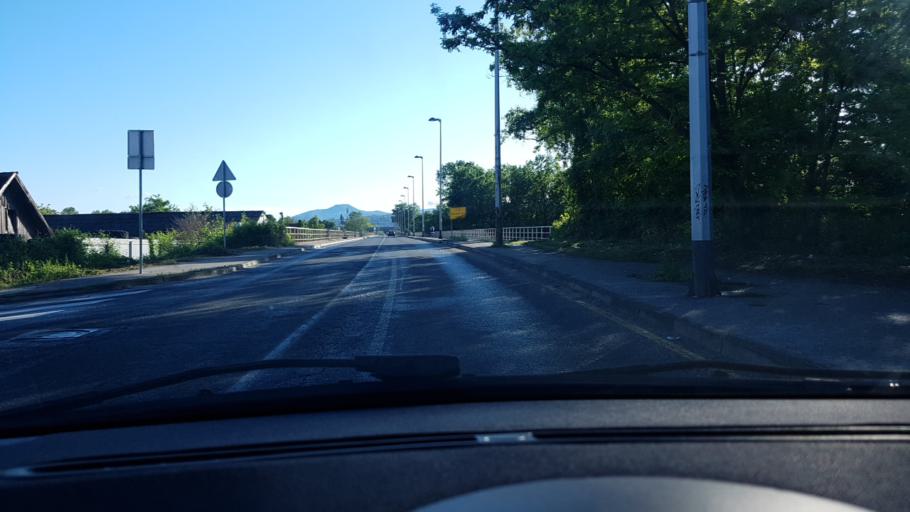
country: HR
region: Zagrebacka
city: Bestovje
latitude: 45.8149
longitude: 15.8347
